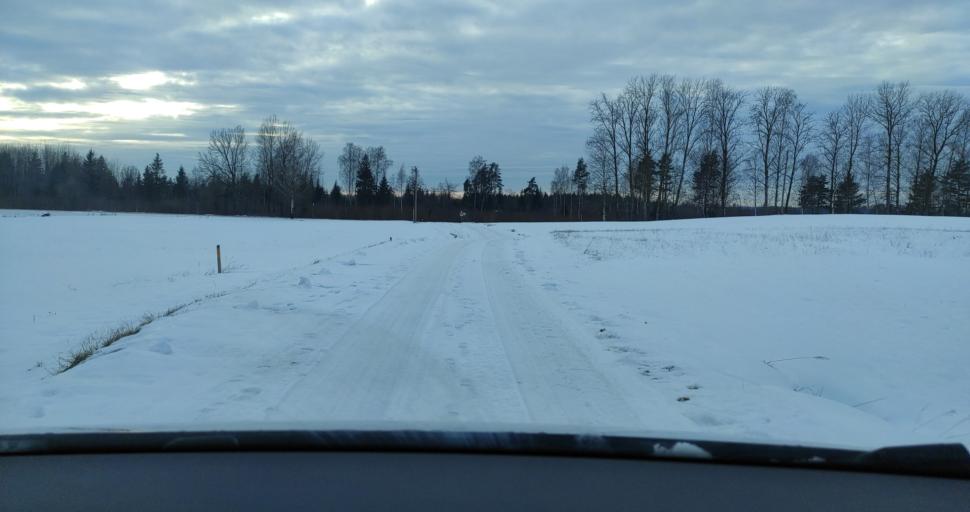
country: LV
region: Kuldigas Rajons
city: Kuldiga
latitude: 56.9410
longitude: 22.0065
